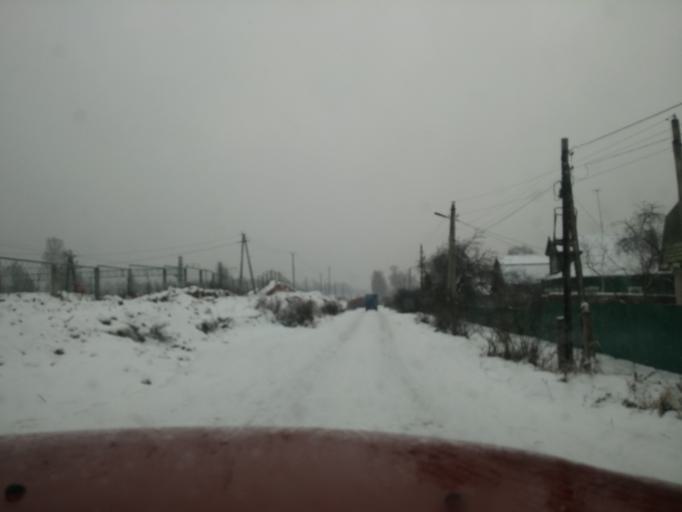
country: RU
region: Tverskaya
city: Novozavidovskiy
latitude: 56.5491
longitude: 36.4411
